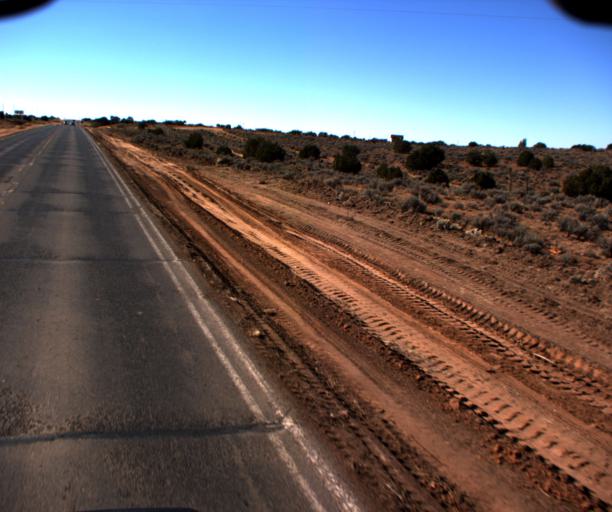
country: US
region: Arizona
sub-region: Apache County
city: Ganado
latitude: 35.7114
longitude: -109.5030
